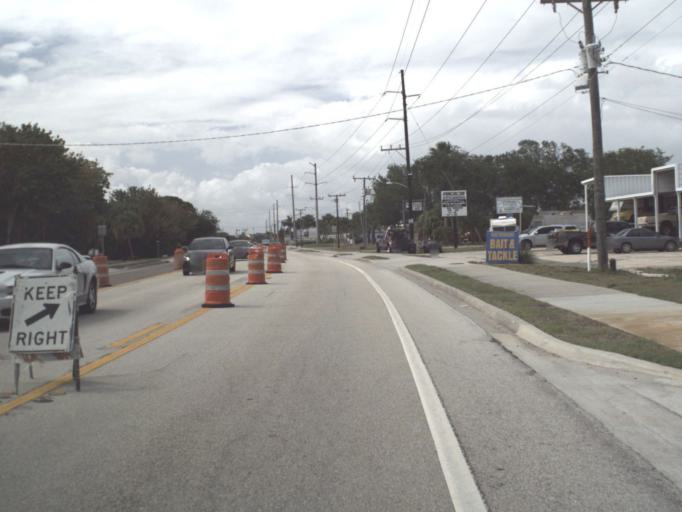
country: US
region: Florida
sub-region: Brevard County
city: Indian Harbour Beach
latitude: 28.1553
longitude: -80.6004
